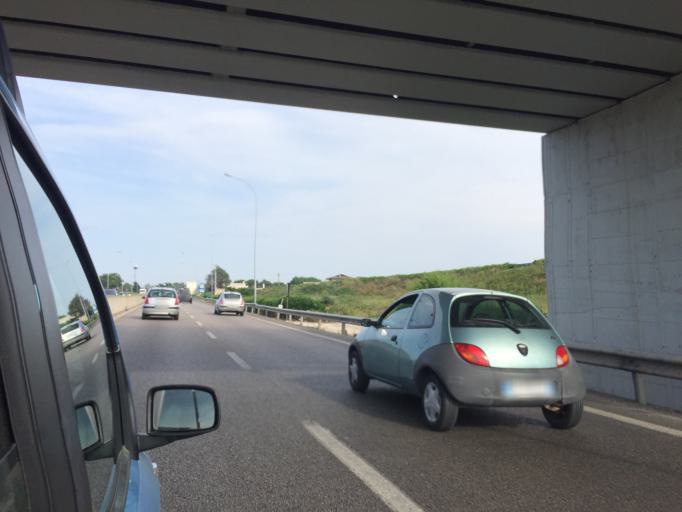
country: IT
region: Apulia
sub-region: Provincia di Bari
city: Triggiano
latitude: 41.0961
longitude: 16.9420
